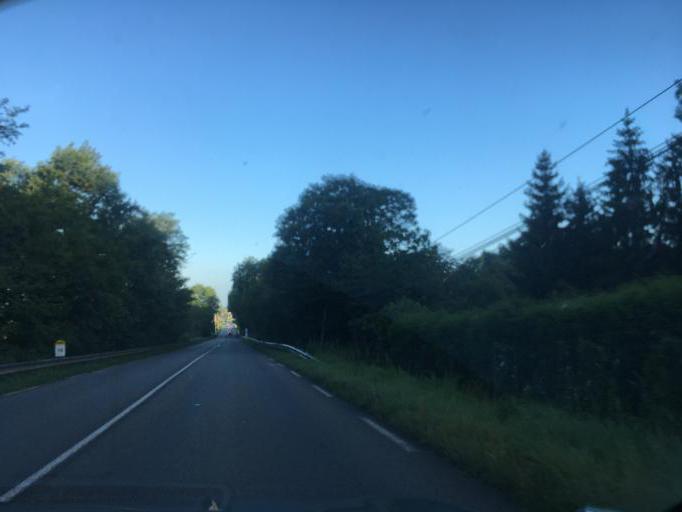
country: FR
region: Aquitaine
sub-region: Departement des Pyrenees-Atlantiques
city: Soumoulou
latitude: 43.2625
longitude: -0.1755
